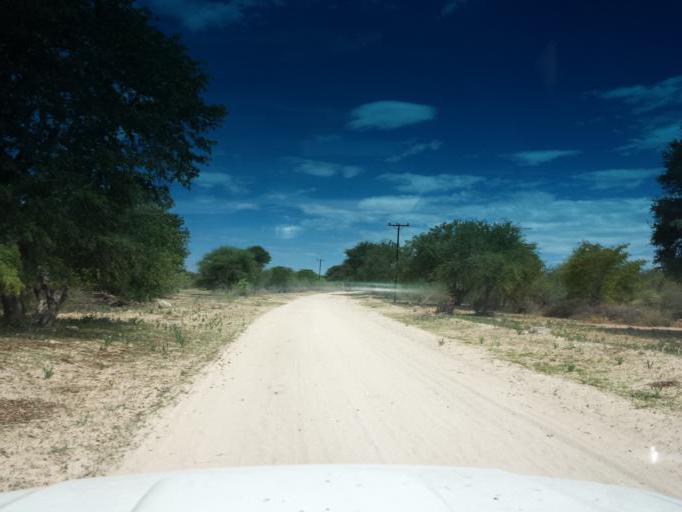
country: BW
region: North West
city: Shakawe
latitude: -18.7466
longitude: 22.1848
